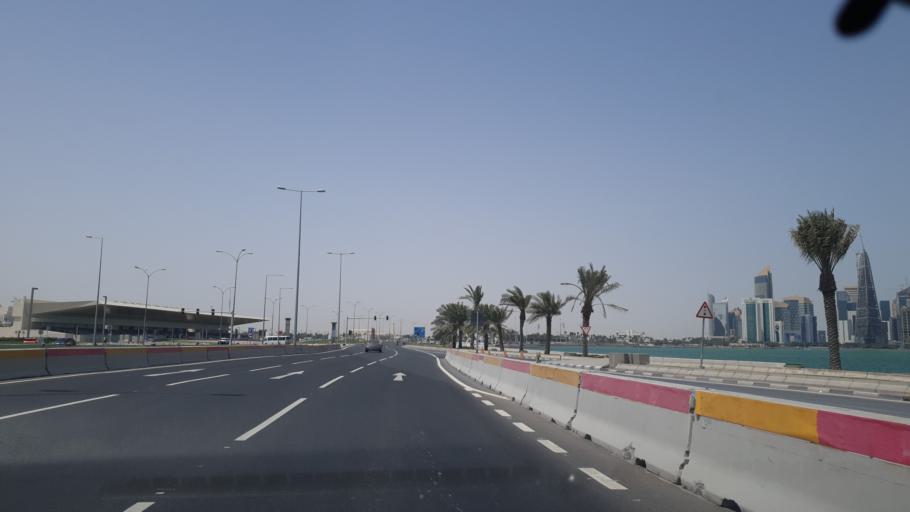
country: QA
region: Baladiyat ad Dawhah
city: Doha
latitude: 25.2968
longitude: 51.5211
